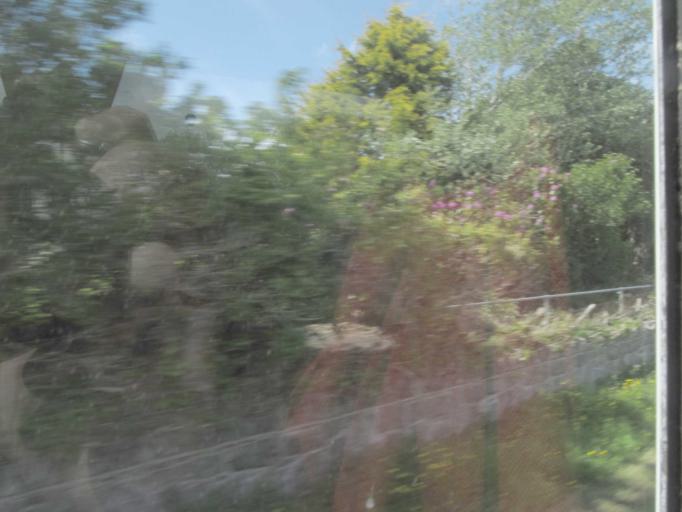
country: GB
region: Northern Ireland
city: Bushmills
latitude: 55.2006
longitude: -6.5278
